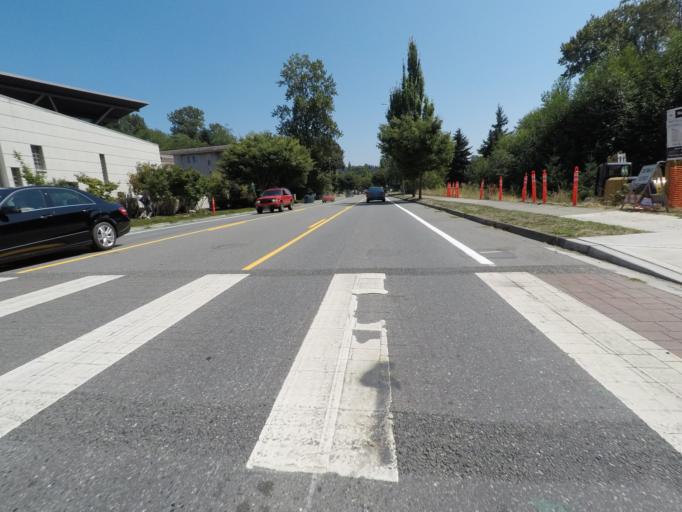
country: US
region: Washington
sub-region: King County
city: Inglewood-Finn Hill
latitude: 47.7054
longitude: -122.2179
